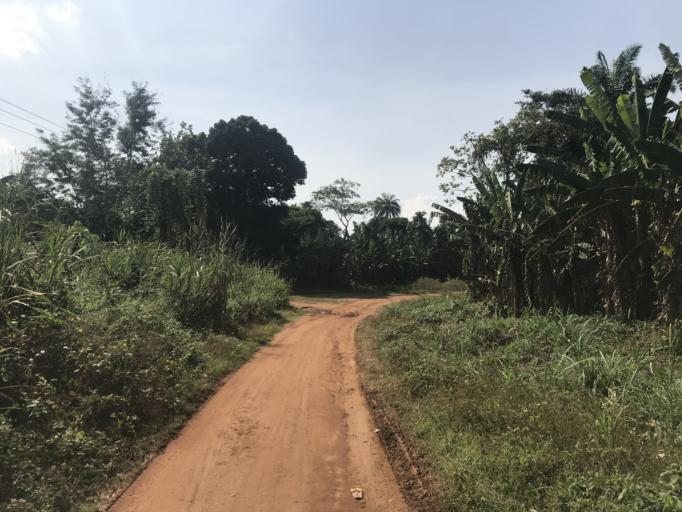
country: NG
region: Osun
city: Osu
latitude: 7.6336
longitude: 4.6671
